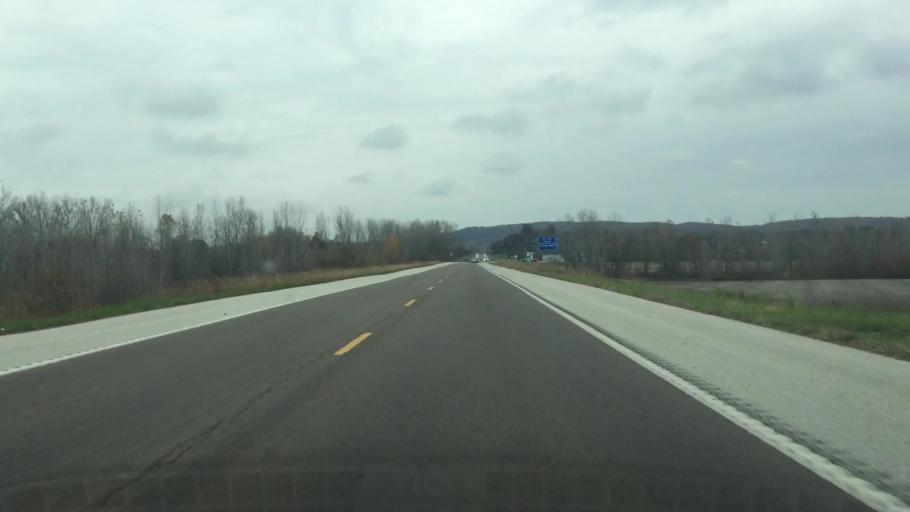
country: US
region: Missouri
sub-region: Gasconade County
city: Hermann
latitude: 38.7237
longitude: -91.4444
